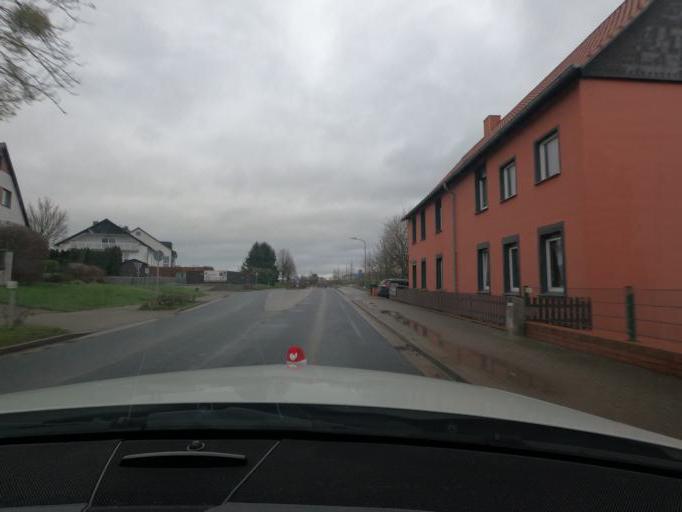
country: DE
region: Lower Saxony
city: Seesen
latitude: 51.8528
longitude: 10.1290
